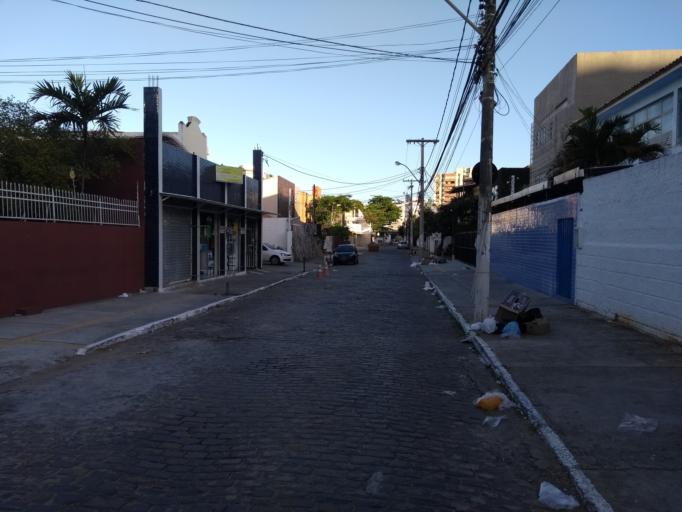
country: BR
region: Bahia
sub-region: Salvador
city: Salvador
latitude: -13.0097
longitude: -38.4913
